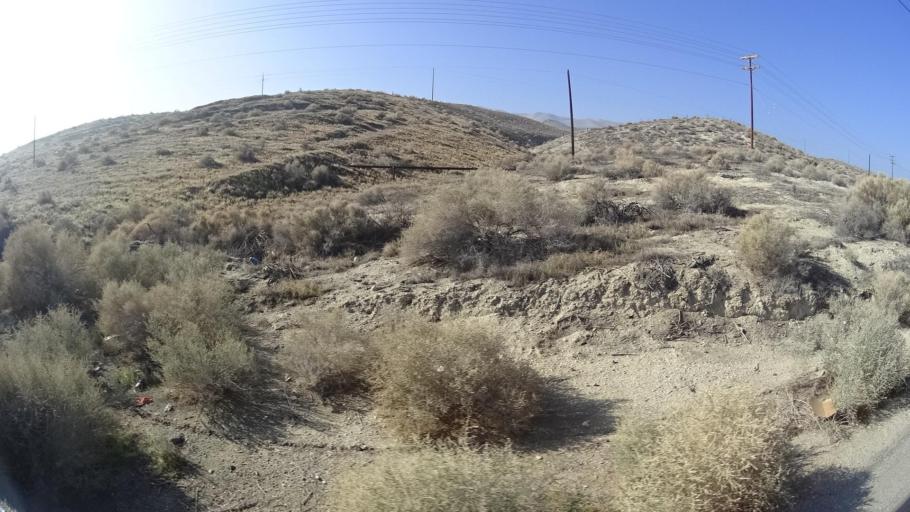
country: US
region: California
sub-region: Kern County
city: Taft Heights
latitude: 35.1975
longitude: -119.5889
